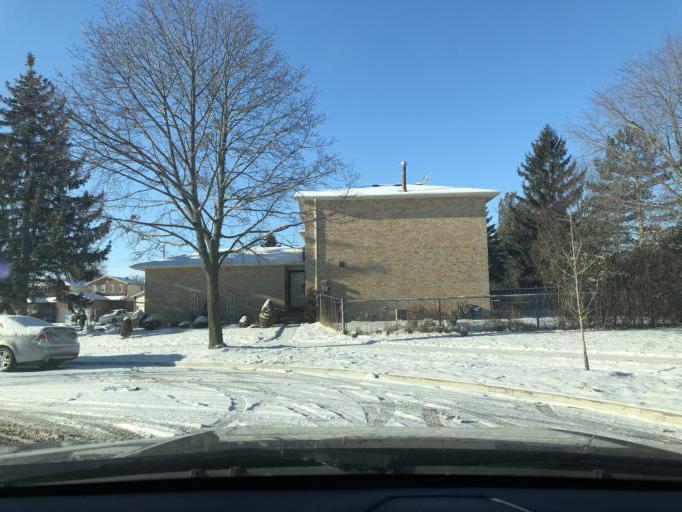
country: CA
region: Ontario
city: Pickering
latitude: 43.7847
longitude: -79.1358
